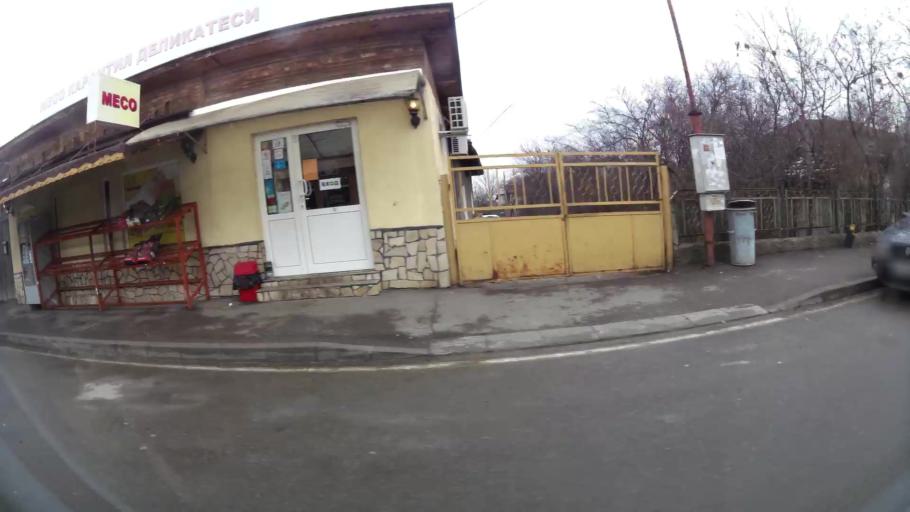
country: BG
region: Sofiya
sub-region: Obshtina Bozhurishte
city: Bozhurishte
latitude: 42.6964
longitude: 23.2263
